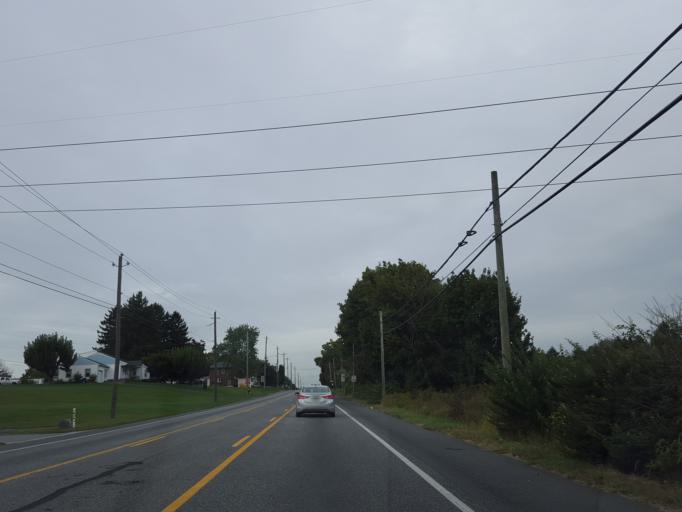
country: US
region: Pennsylvania
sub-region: York County
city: Weigelstown
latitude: 39.9287
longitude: -76.8408
